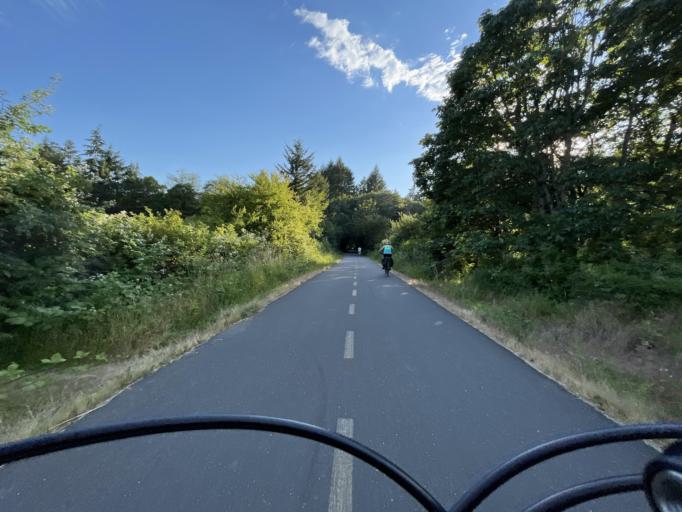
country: CA
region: British Columbia
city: Colwood
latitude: 48.4596
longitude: -123.4580
